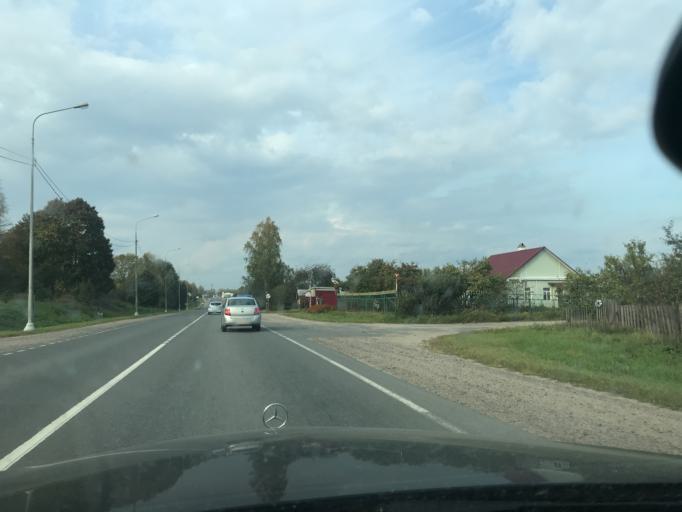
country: RU
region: Pskov
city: Ostrov
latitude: 57.3057
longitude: 28.3687
